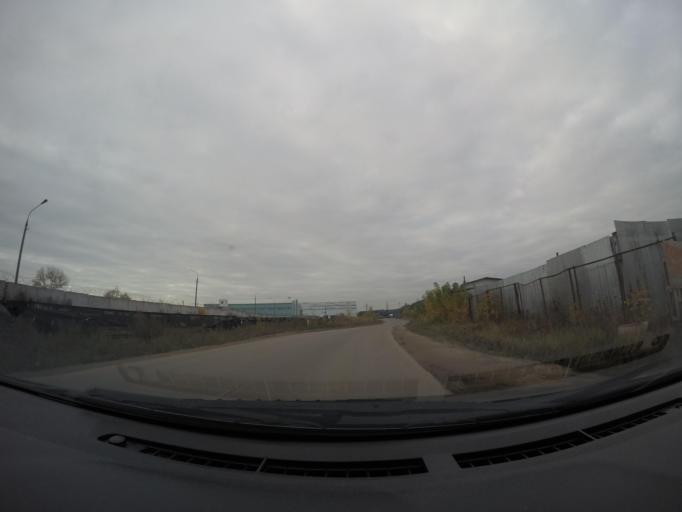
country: RU
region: Moskovskaya
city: Staraya Kupavna
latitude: 55.7936
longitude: 38.1834
